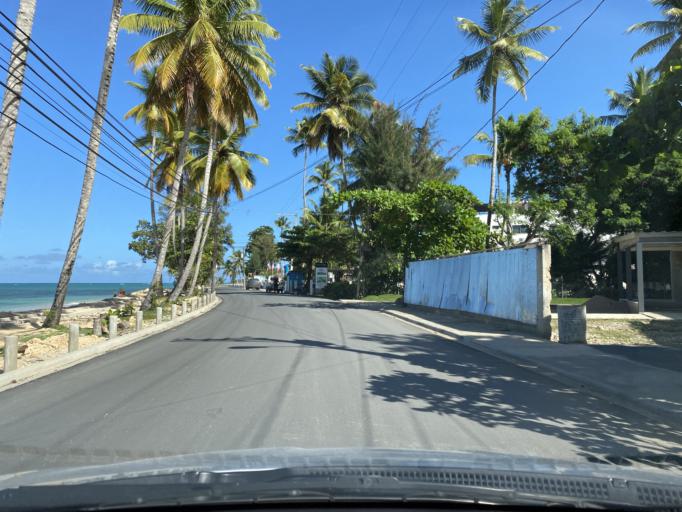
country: DO
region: Samana
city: Las Terrenas
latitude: 19.3224
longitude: -69.5353
